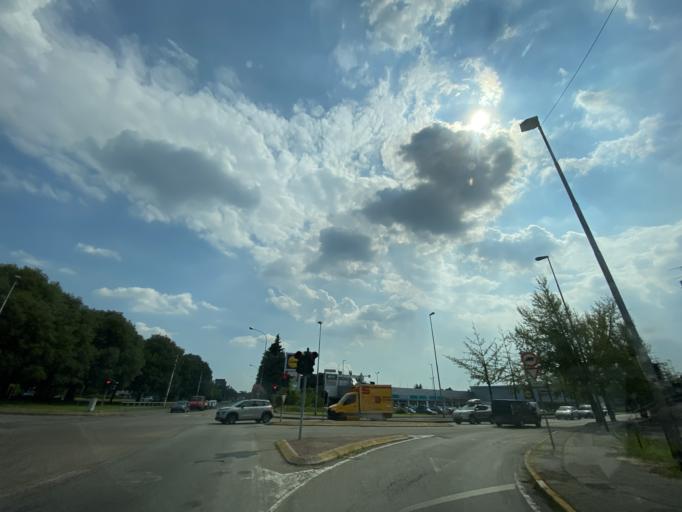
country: IT
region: Lombardy
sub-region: Provincia di Monza e Brianza
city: Nova Milanese
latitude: 45.5975
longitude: 9.1996
